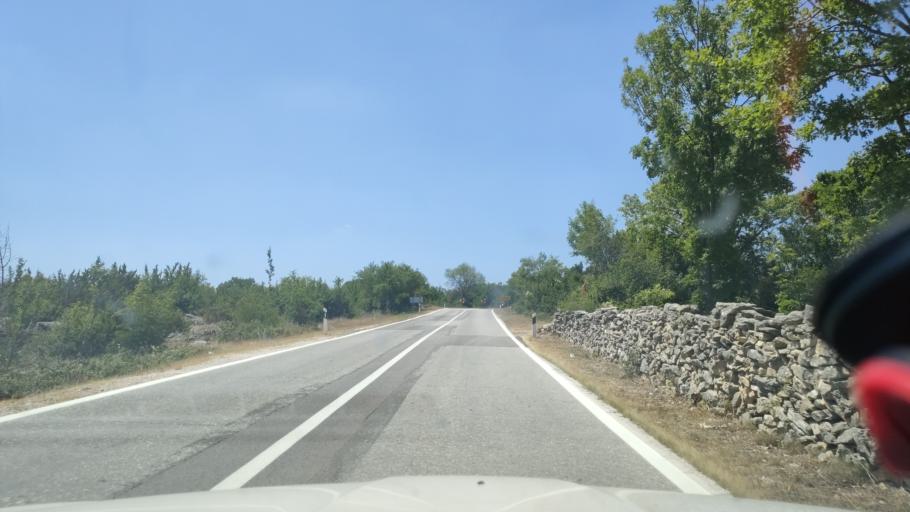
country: HR
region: Sibensko-Kniniska
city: Kistanje
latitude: 44.0056
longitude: 16.0014
